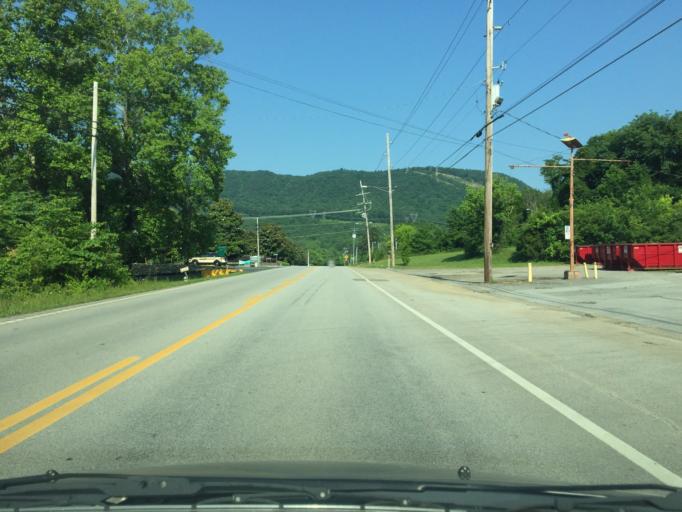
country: US
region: Tennessee
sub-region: Hamilton County
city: Lookout Mountain
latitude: 35.0245
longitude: -85.3964
